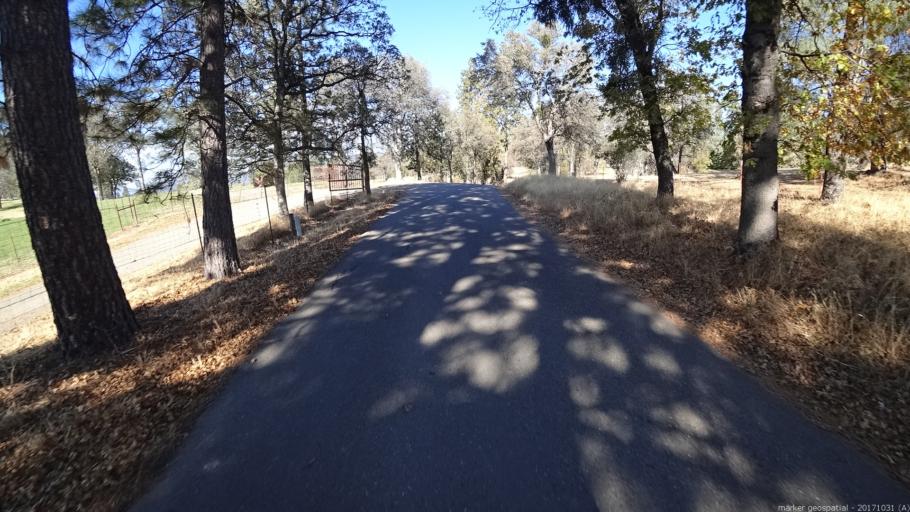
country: US
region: California
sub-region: Shasta County
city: Shingletown
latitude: 40.4443
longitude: -121.8369
